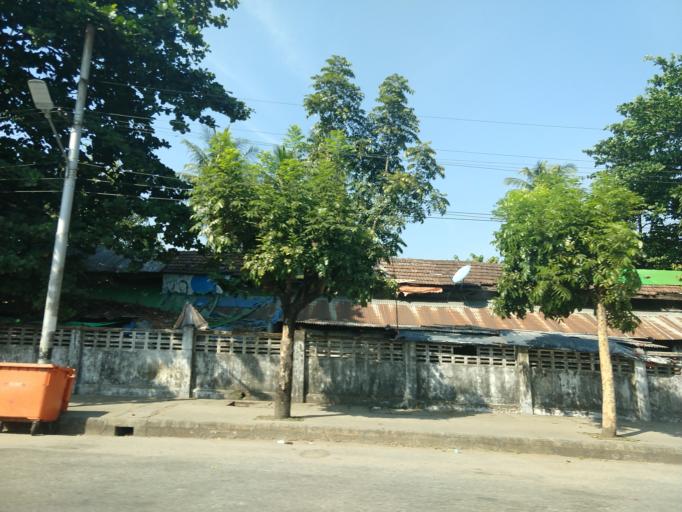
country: MM
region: Yangon
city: Yangon
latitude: 16.7695
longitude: 96.1688
